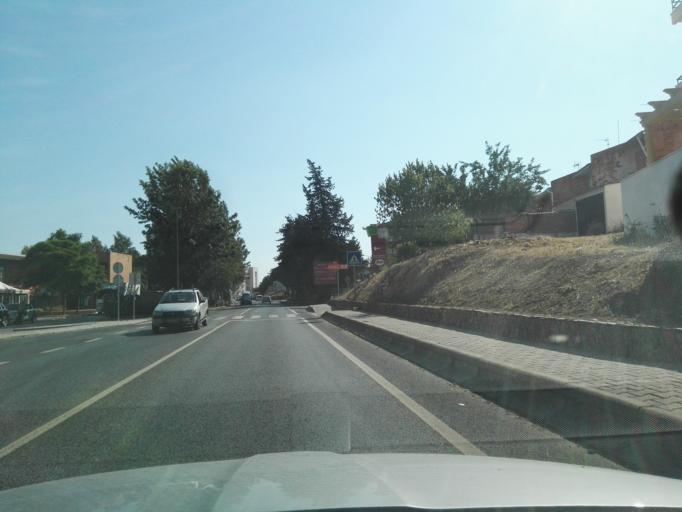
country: PT
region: Lisbon
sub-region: Vila Franca de Xira
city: Povoa de Santa Iria
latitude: 38.8692
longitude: -9.0577
